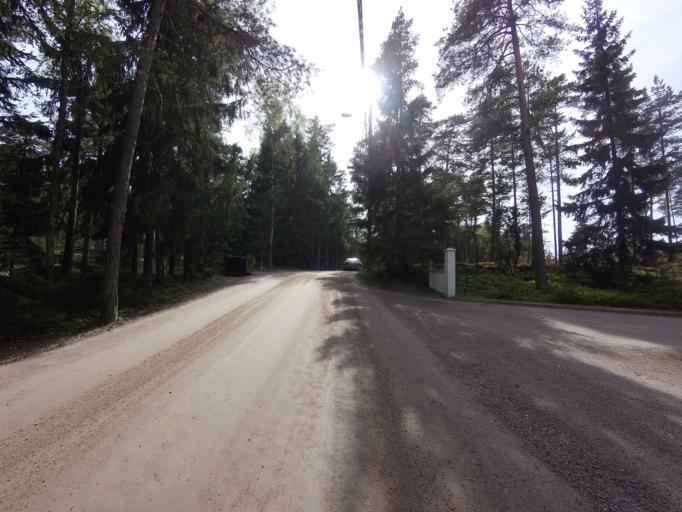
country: FI
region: Uusimaa
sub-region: Helsinki
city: Koukkuniemi
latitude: 60.1170
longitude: 24.7245
